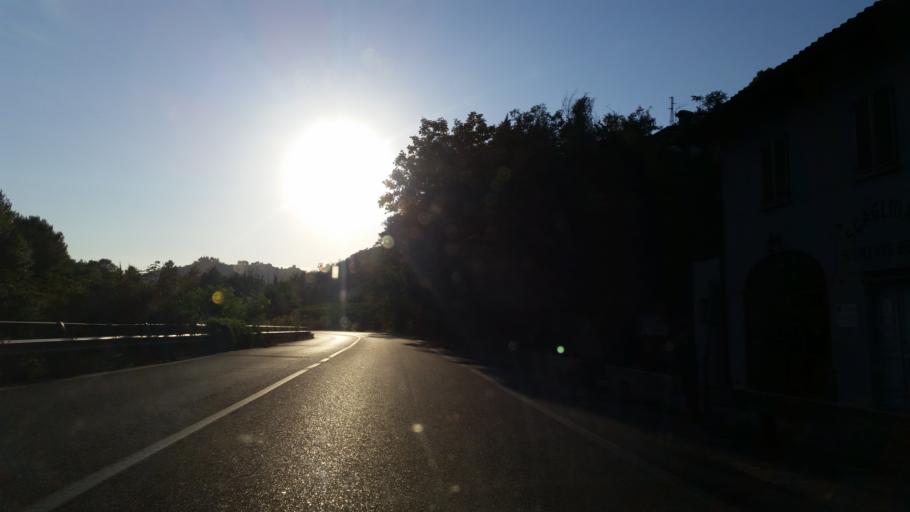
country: IT
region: Piedmont
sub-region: Provincia di Cuneo
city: Santo Stefano Belbo
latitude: 44.7132
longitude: 8.2582
